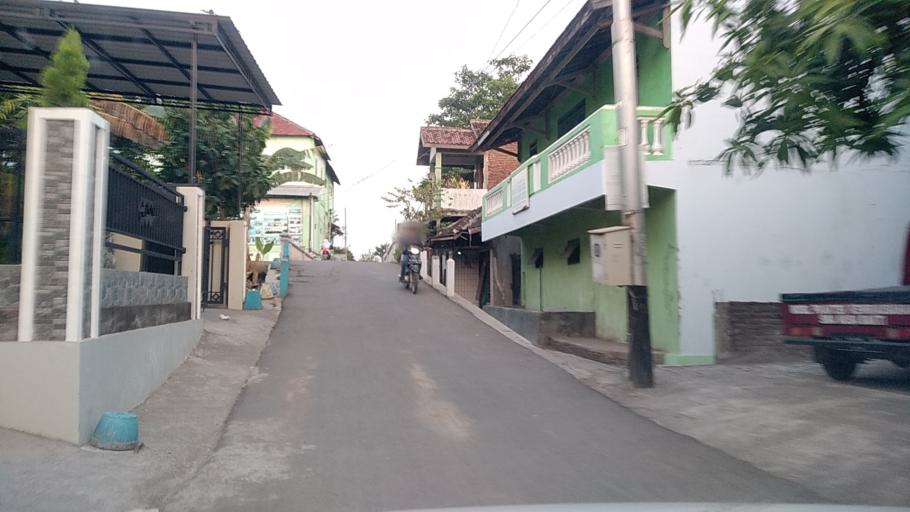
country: ID
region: Central Java
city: Semarang
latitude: -6.9710
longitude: 110.3071
